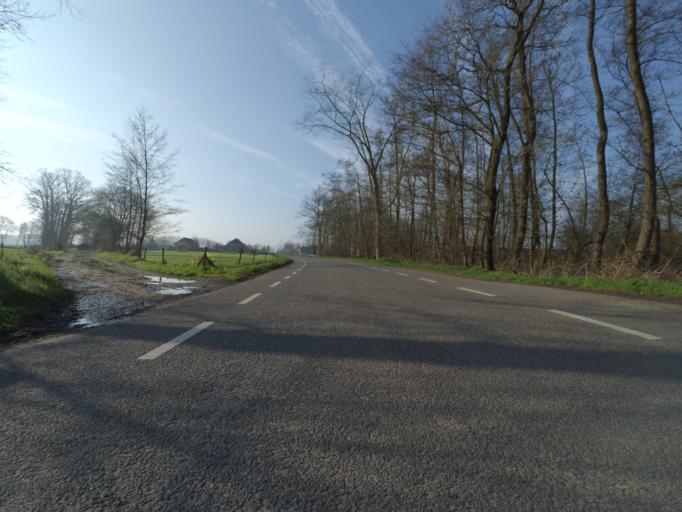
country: NL
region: Gelderland
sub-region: Gemeente Barneveld
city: Terschuur
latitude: 52.1541
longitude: 5.4969
